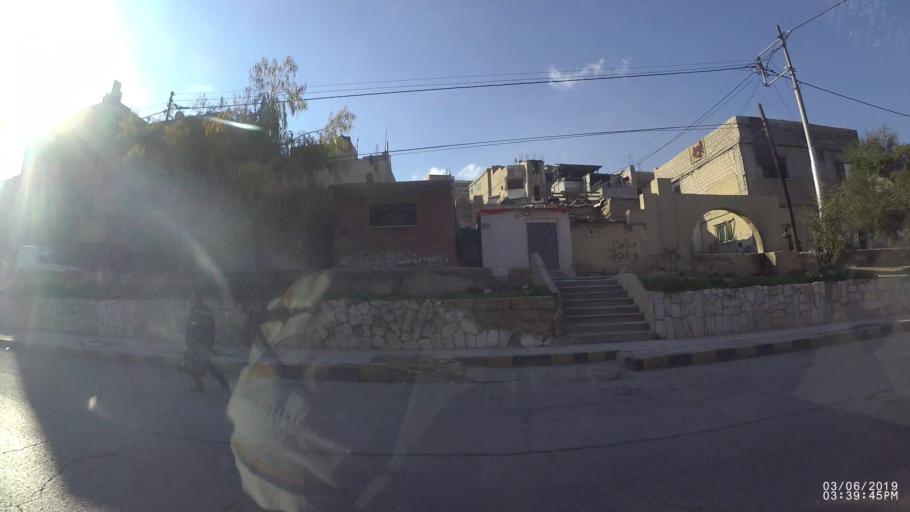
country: JO
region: Amman
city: Amman
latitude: 31.9654
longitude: 35.9616
